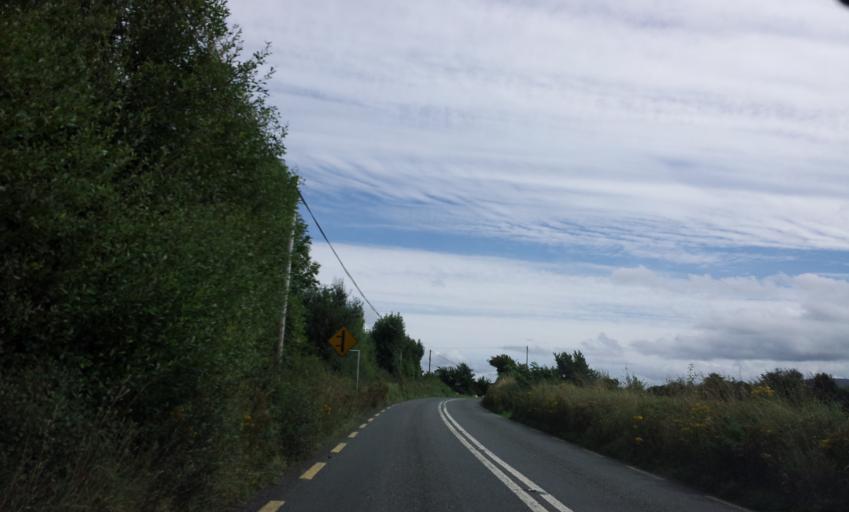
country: IE
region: Munster
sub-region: Ciarrai
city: Killorglin
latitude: 52.0826
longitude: -9.6678
